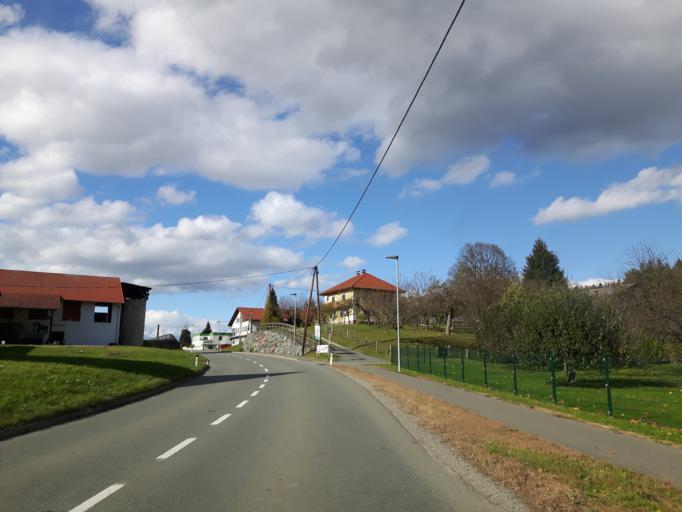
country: AT
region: Styria
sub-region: Politischer Bezirk Leibnitz
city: Gleinstatten
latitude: 46.7622
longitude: 15.4003
